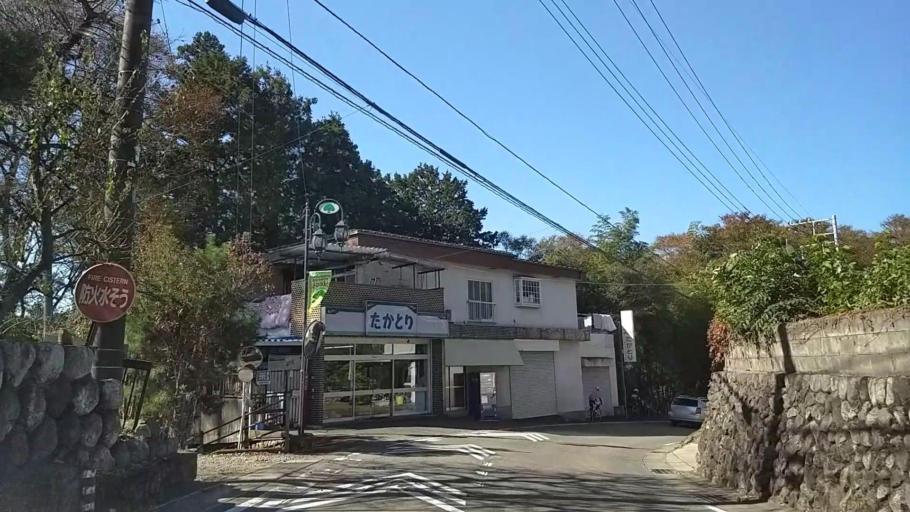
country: JP
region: Yamanashi
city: Uenohara
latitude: 35.6398
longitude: 139.1032
